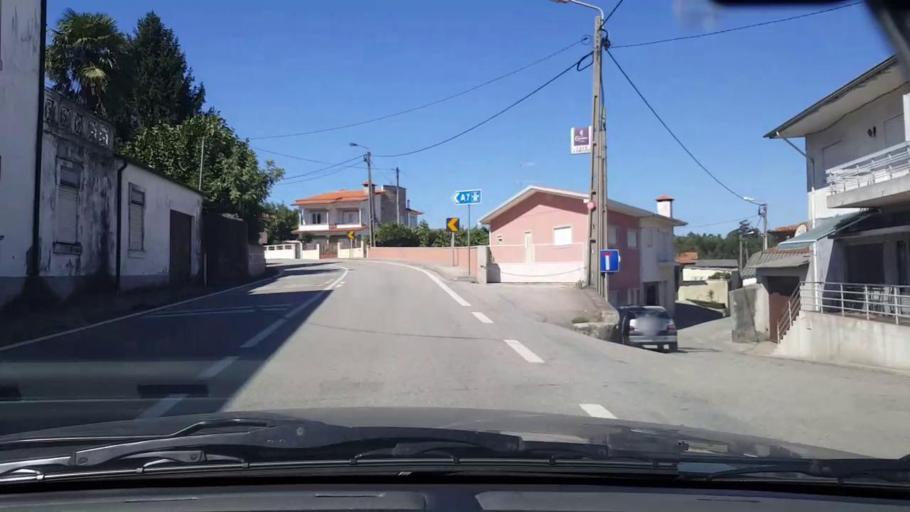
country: PT
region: Porto
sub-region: Maia
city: Gemunde
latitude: 41.3397
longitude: -8.6391
